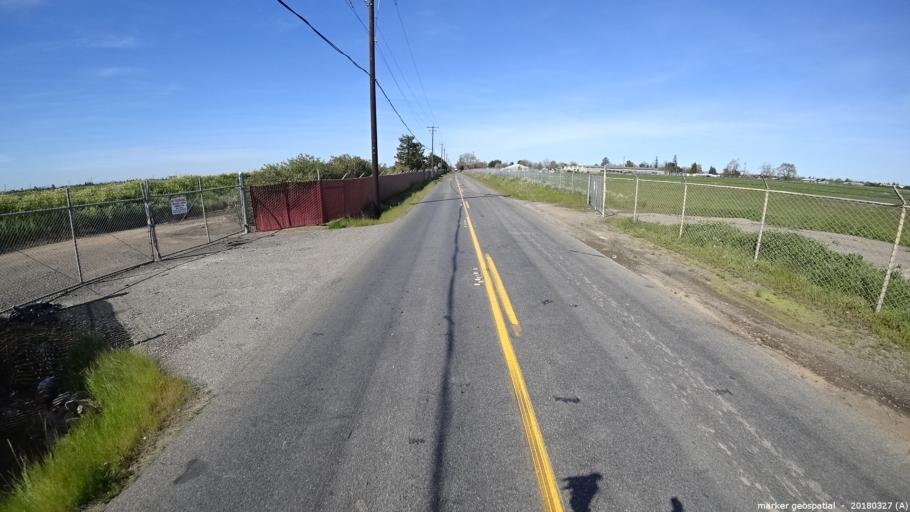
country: US
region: California
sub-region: Sacramento County
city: Rosemont
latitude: 38.5253
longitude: -121.3448
